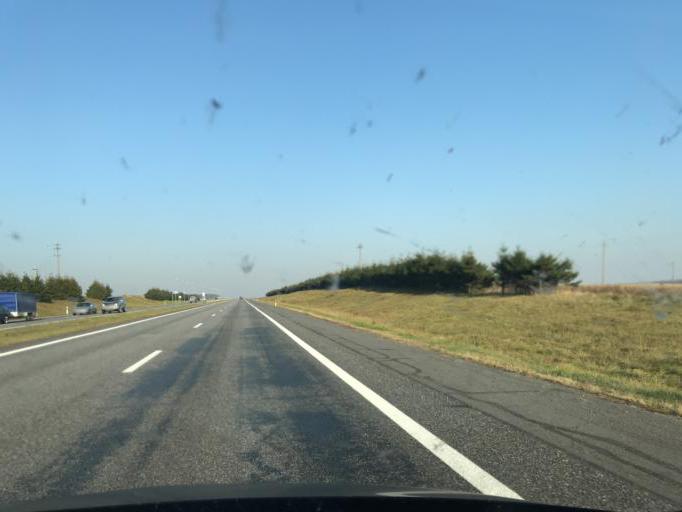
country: BY
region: Minsk
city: Haradzyeya
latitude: 53.3521
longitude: 26.4607
